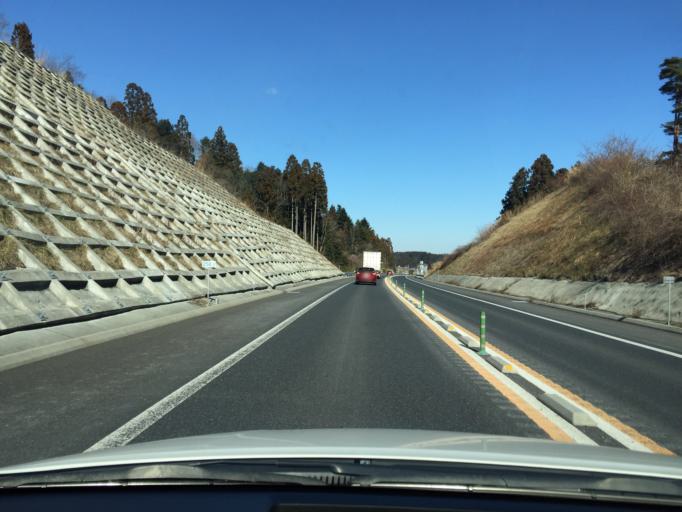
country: JP
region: Miyagi
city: Marumori
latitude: 37.7189
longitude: 140.9183
